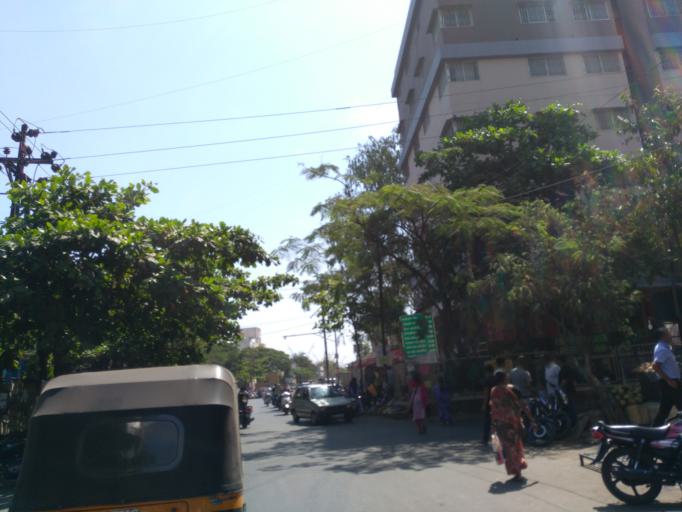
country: IN
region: Maharashtra
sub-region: Pune Division
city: Pune
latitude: 18.4545
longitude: 73.8531
